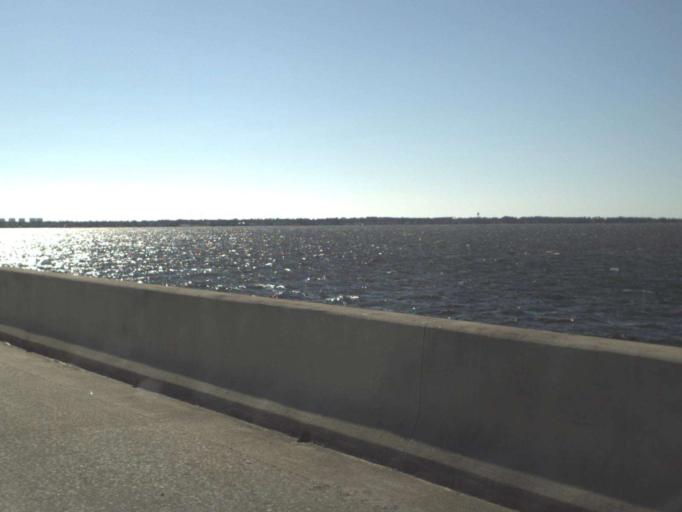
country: US
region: Florida
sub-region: Santa Rosa County
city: Oriole Beach
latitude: 30.4234
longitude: -87.0920
